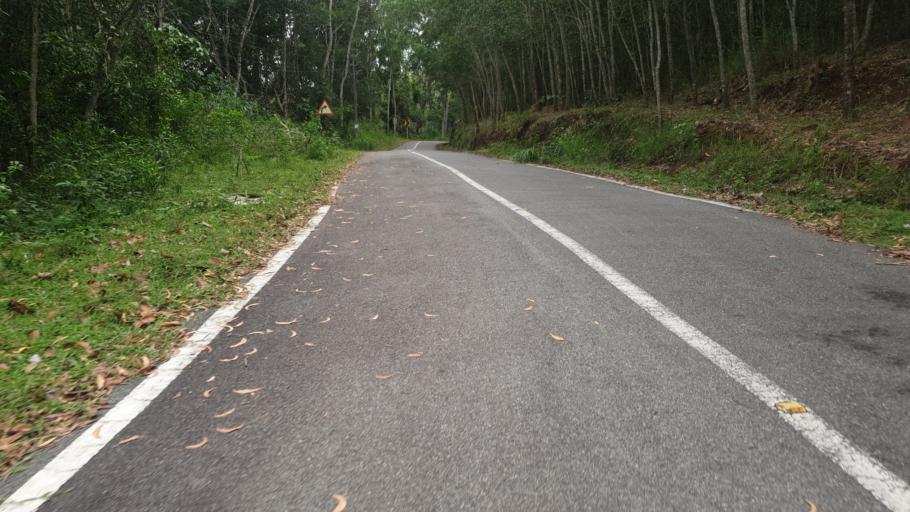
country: IN
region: Kerala
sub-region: Thiruvananthapuram
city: Nedumangad
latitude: 8.6325
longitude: 77.1142
